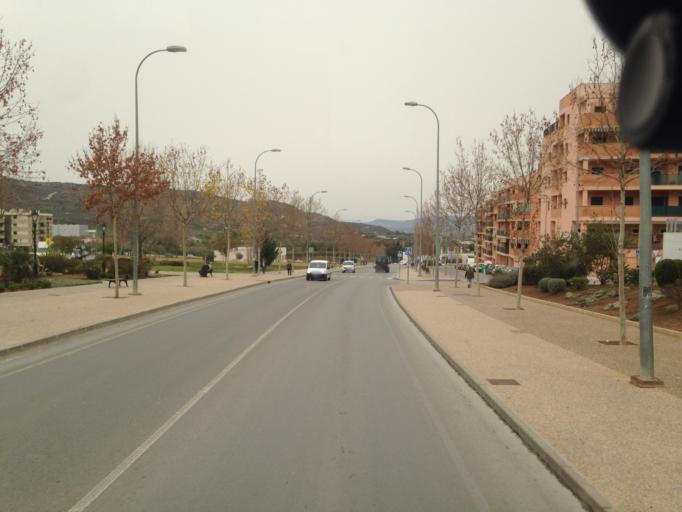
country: ES
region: Andalusia
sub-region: Provincia de Malaga
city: Antequera
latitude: 37.0238
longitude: -4.5705
